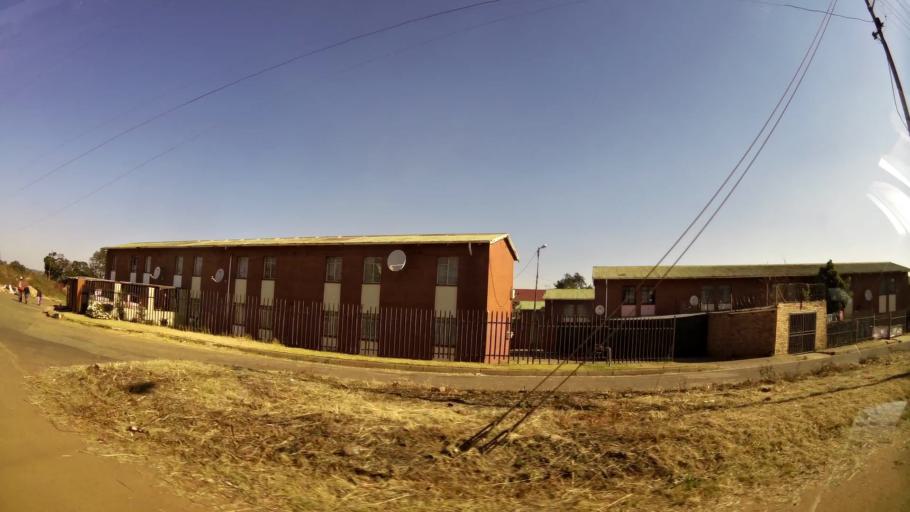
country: ZA
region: Gauteng
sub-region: City of Johannesburg Metropolitan Municipality
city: Johannesburg
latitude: -26.1930
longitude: 27.9773
